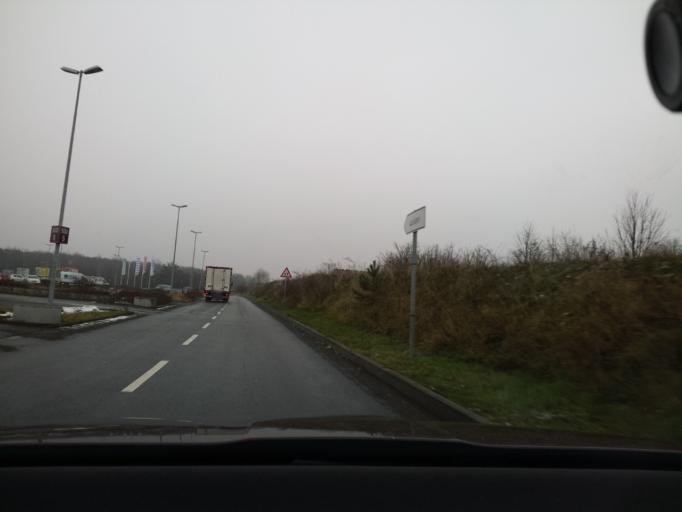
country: DE
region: Brandenburg
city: Wildau
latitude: 52.3118
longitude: 13.6086
